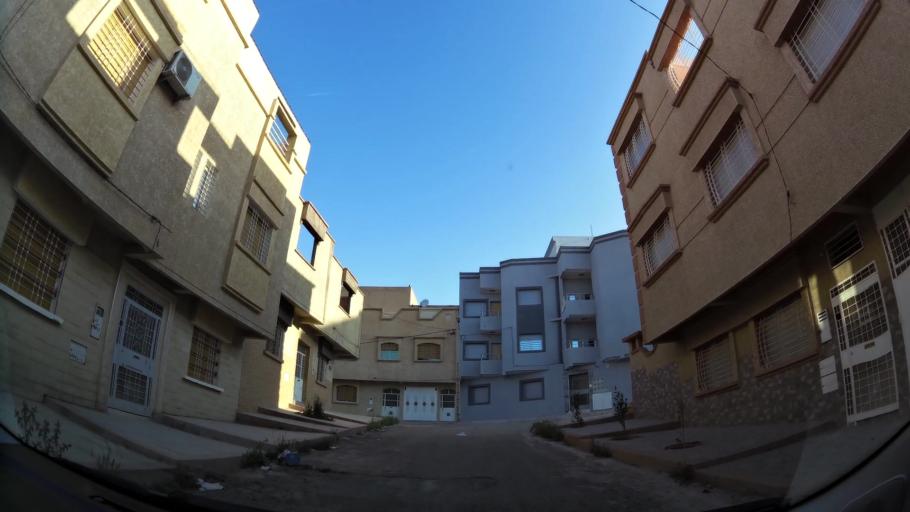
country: MA
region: Oriental
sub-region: Oujda-Angad
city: Oujda
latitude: 34.6754
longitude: -1.9402
